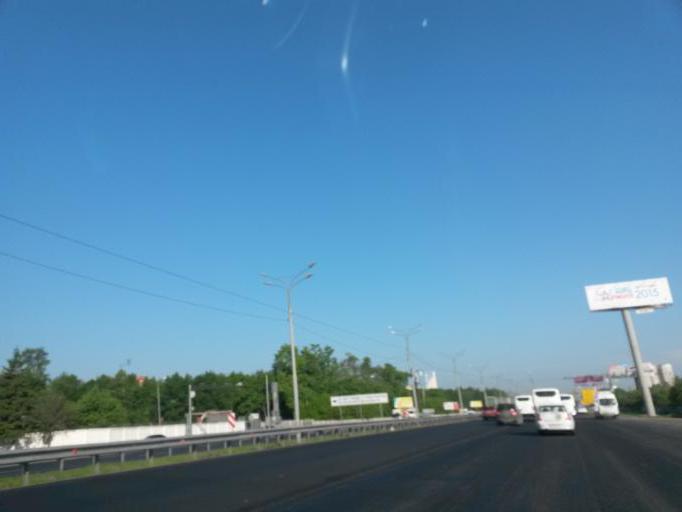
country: RU
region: Moskovskaya
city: Razvilka
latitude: 55.5861
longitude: 37.7392
